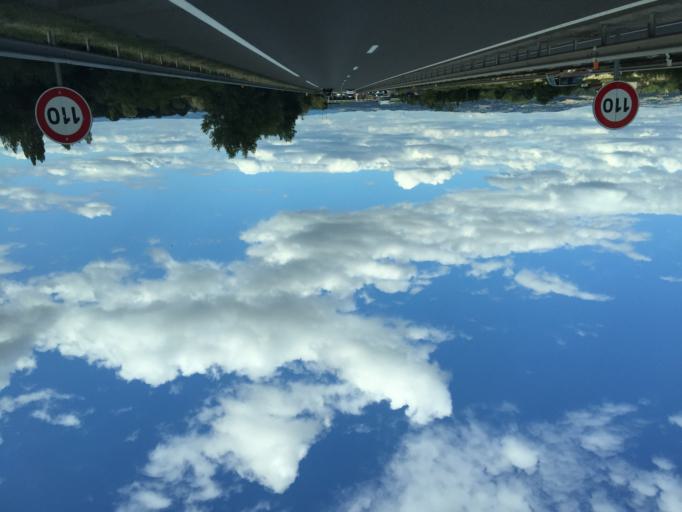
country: FR
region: Rhone-Alpes
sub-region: Departement de la Loire
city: Saint-Cyprien
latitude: 45.5636
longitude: 4.2347
